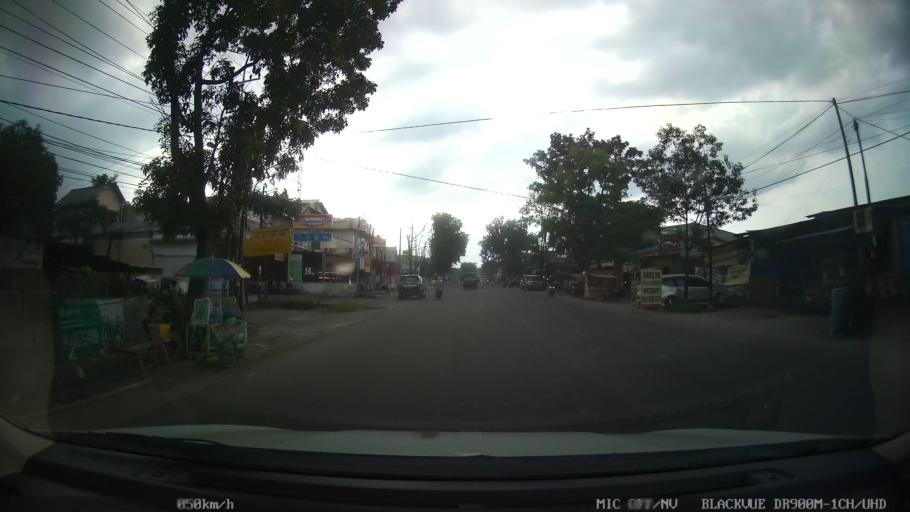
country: ID
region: North Sumatra
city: Sunggal
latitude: 3.5399
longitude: 98.6271
